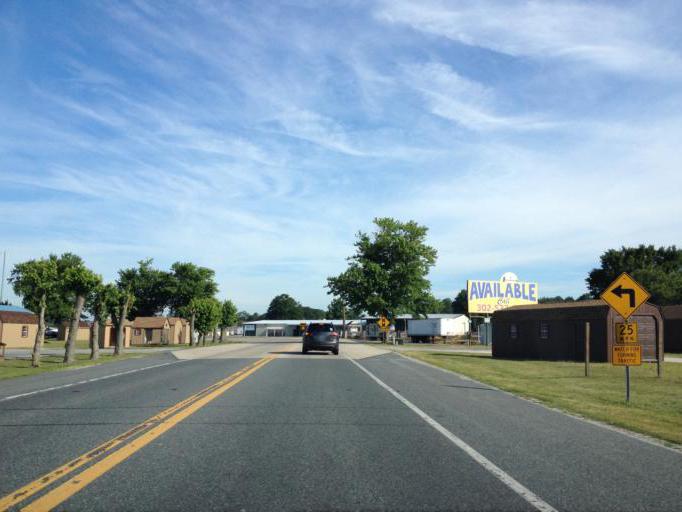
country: US
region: Delaware
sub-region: Sussex County
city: Millsboro
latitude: 38.5661
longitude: -75.2770
